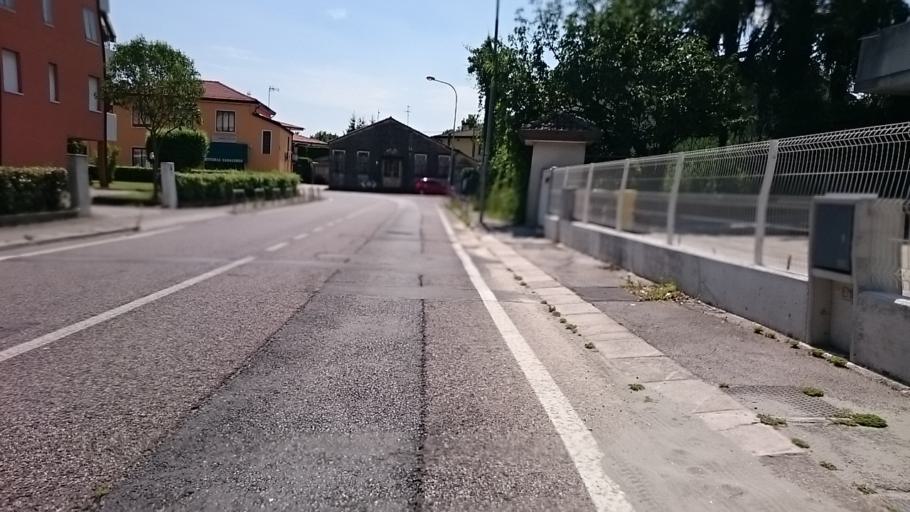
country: IT
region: Veneto
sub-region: Provincia di Padova
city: San Vito
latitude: 45.4199
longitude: 11.9585
